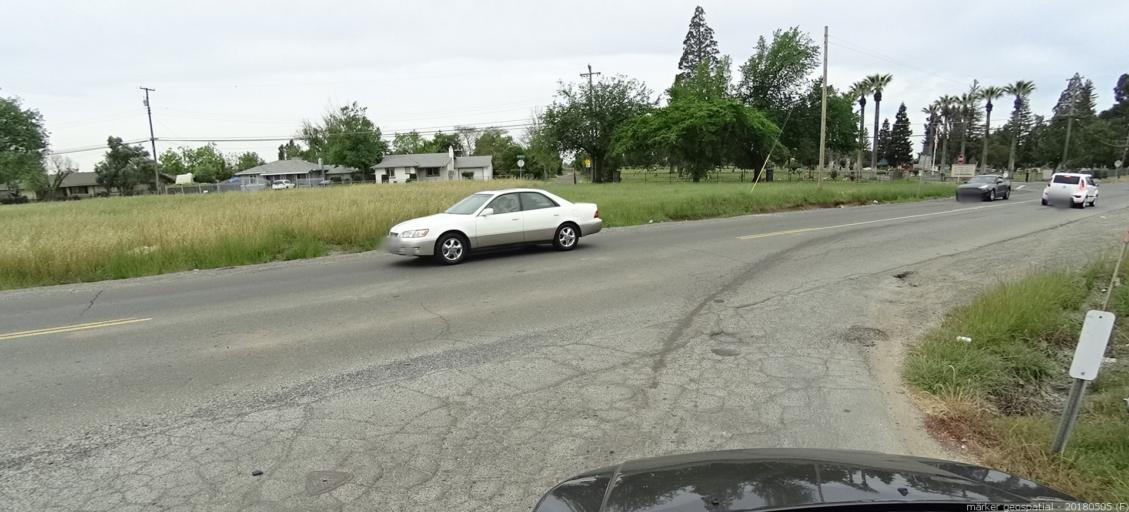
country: US
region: California
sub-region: Sacramento County
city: Rio Linda
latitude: 38.6511
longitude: -121.4378
